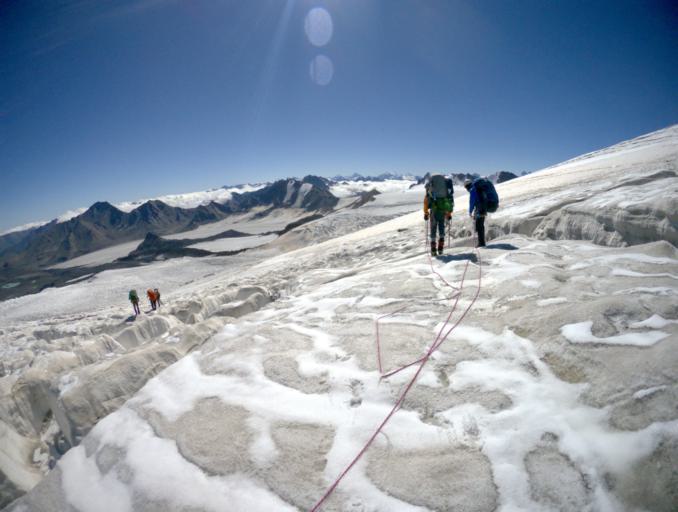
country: RU
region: Kabardino-Balkariya
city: Terskol
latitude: 43.3637
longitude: 42.4978
